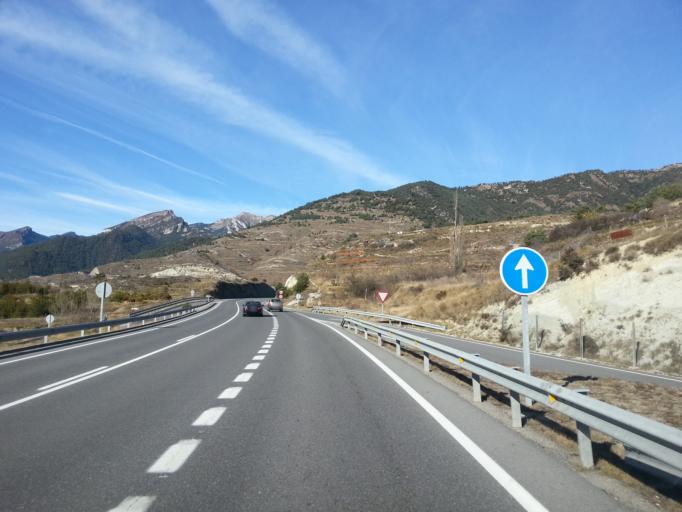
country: ES
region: Catalonia
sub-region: Provincia de Barcelona
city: Baga
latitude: 42.2527
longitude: 1.8673
